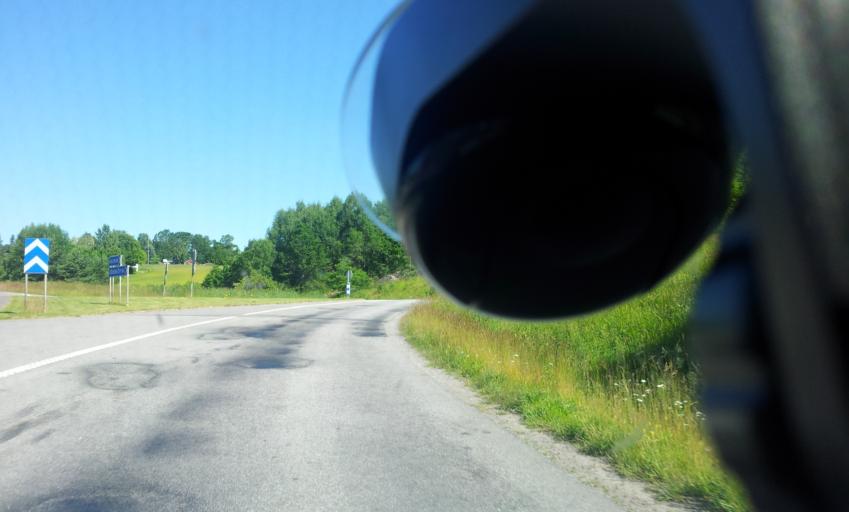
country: SE
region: OEstergoetland
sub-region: Soderkopings Kommun
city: Soederkoeping
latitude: 58.4914
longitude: 16.3091
